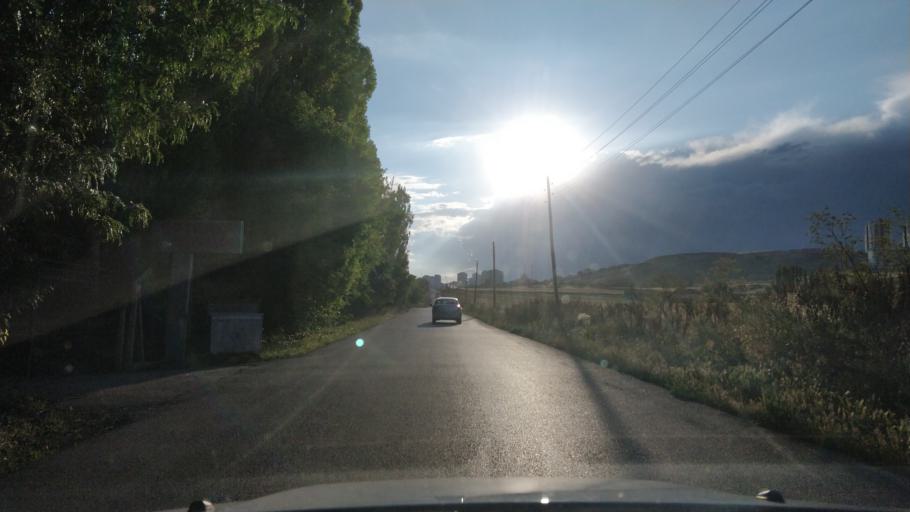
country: TR
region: Ankara
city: Etimesgut
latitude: 39.8260
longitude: 32.5682
